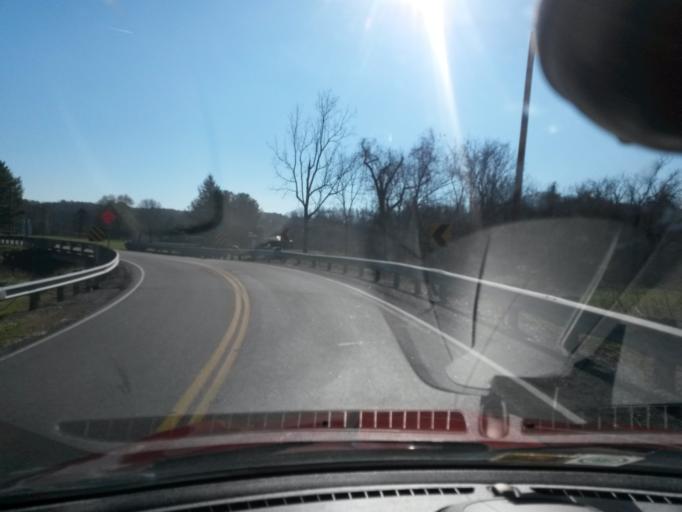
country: US
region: Virginia
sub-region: City of Bedford
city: Bedford
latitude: 37.3931
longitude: -79.5556
